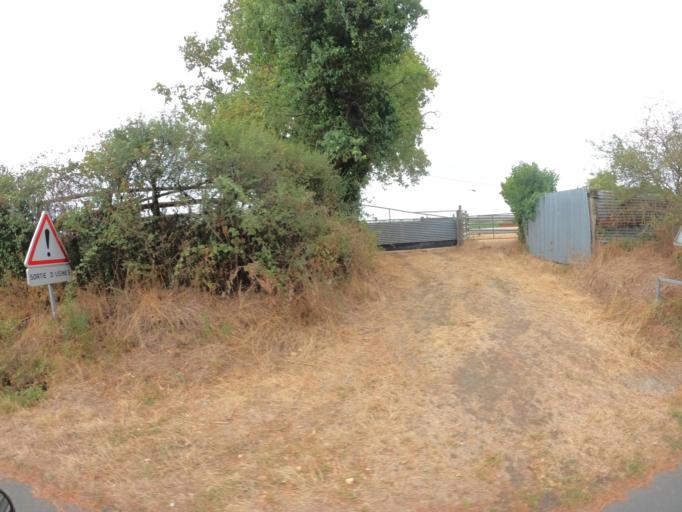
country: FR
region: Pays de la Loire
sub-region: Departement de Maine-et-Loire
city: La Seguiniere
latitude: 47.0492
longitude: -0.9123
